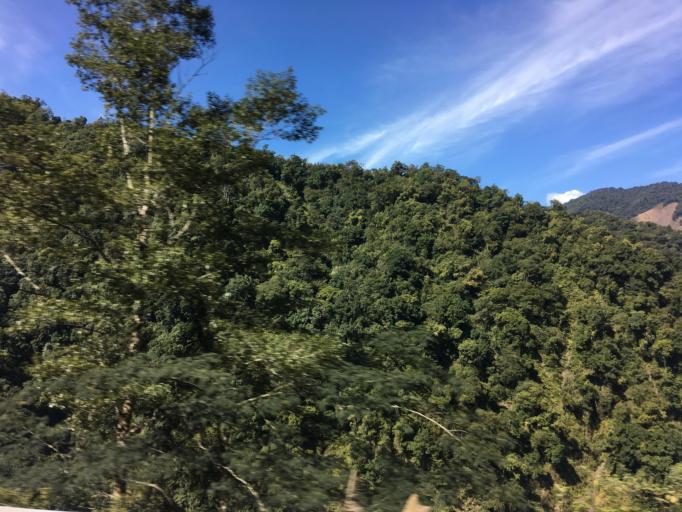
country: TW
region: Taiwan
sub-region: Yilan
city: Yilan
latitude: 24.5384
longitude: 121.5111
